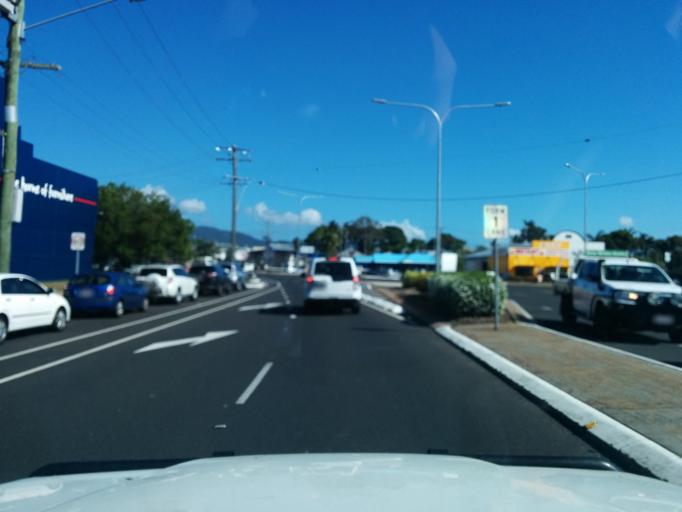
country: AU
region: Queensland
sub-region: Cairns
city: Cairns
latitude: -16.9233
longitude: 145.7678
